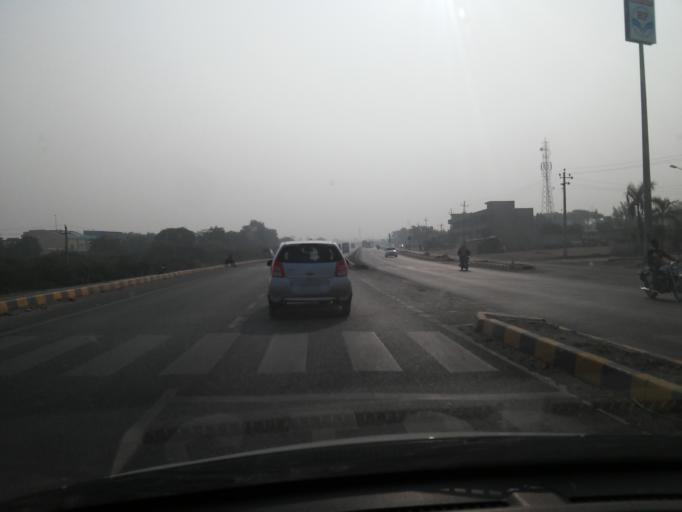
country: IN
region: Gujarat
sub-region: Kachchh
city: Bhuj
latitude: 23.2394
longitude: 69.7199
